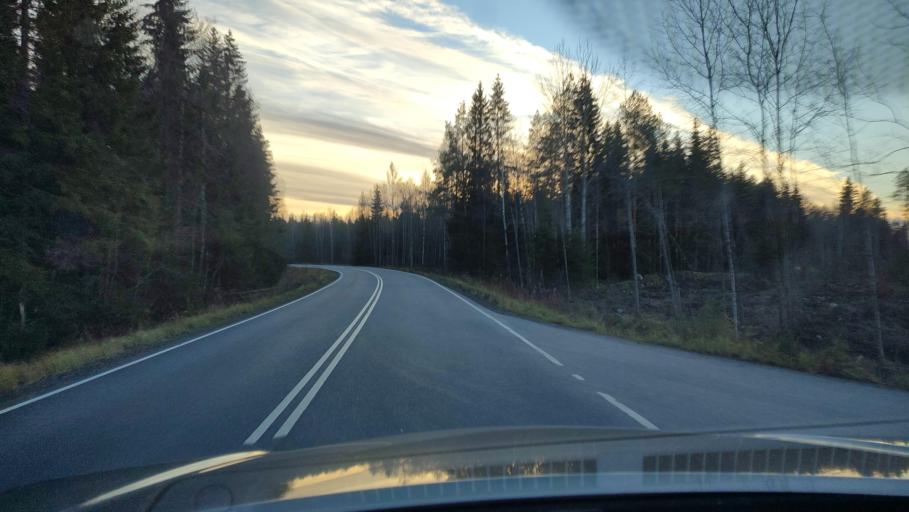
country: FI
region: Southern Ostrobothnia
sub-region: Suupohja
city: Karijoki
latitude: 62.2756
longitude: 21.5686
